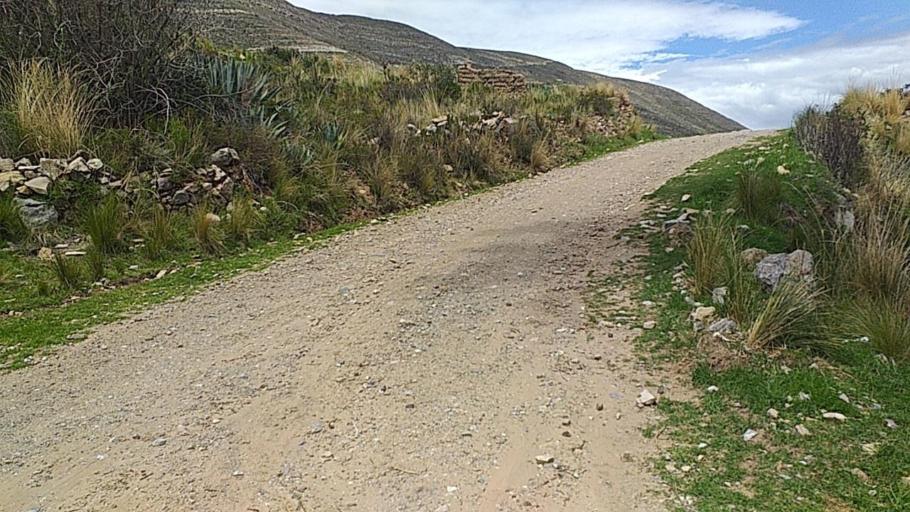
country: BO
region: La Paz
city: Huatajata
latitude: -16.3227
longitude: -68.6638
